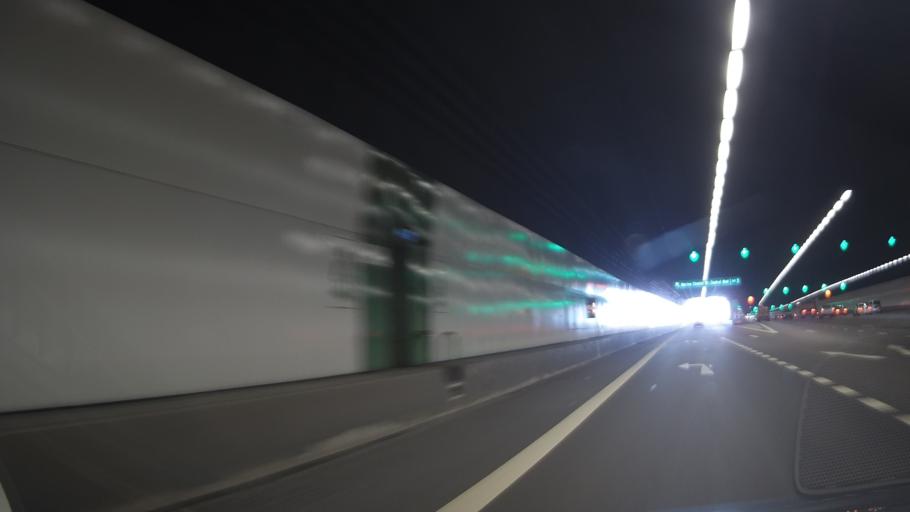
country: SG
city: Singapore
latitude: 1.2833
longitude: 103.8752
